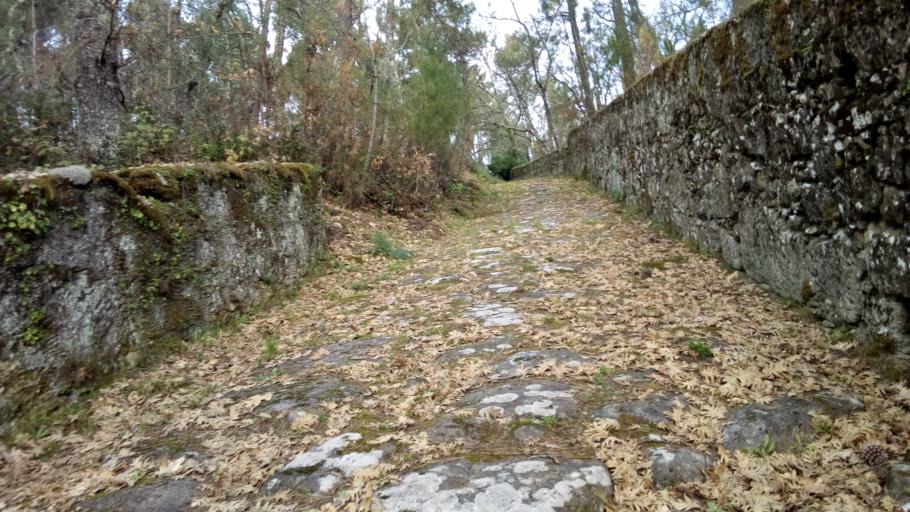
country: PT
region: Guarda
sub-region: Fornos de Algodres
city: Fornos de Algodres
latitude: 40.6116
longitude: -7.5295
